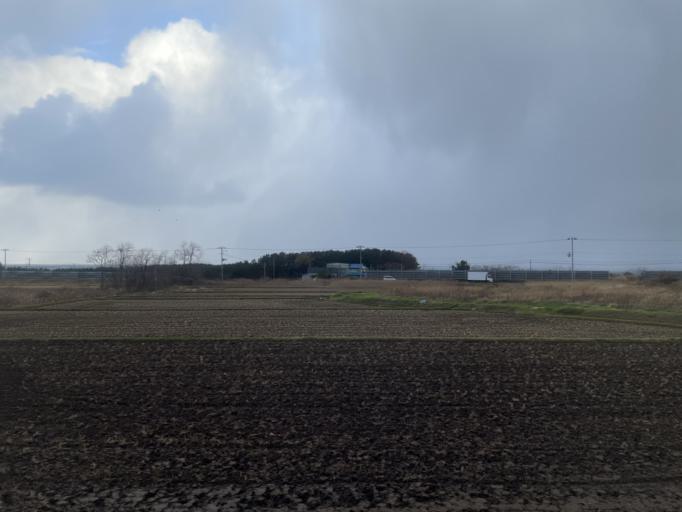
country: JP
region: Aomori
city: Mutsu
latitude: 41.1241
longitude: 141.2647
